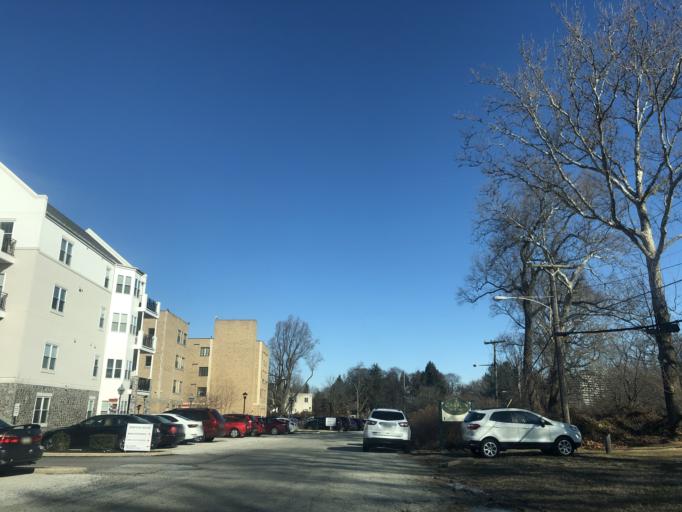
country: US
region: Pennsylvania
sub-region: Montgomery County
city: Bala-Cynwyd
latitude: 39.9957
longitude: -75.2164
